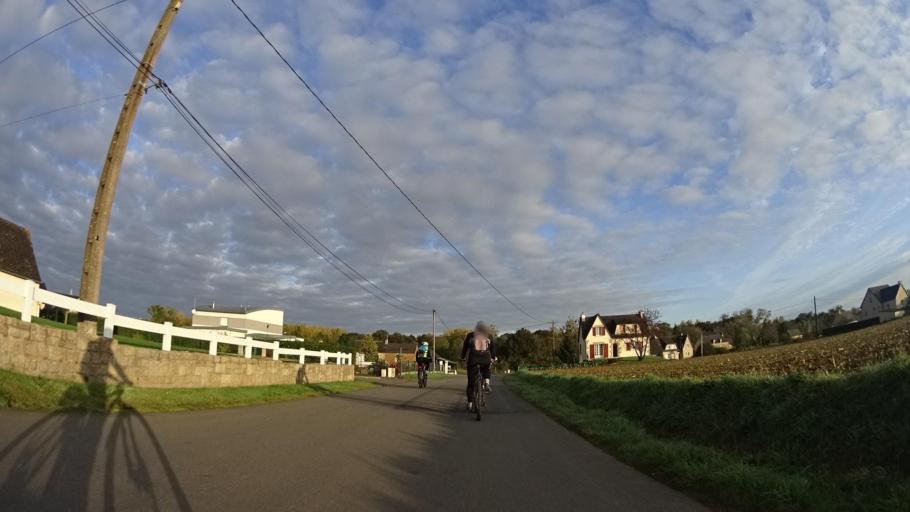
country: FR
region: Brittany
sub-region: Departement des Cotes-d'Armor
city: Evran
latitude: 48.3801
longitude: -1.9695
